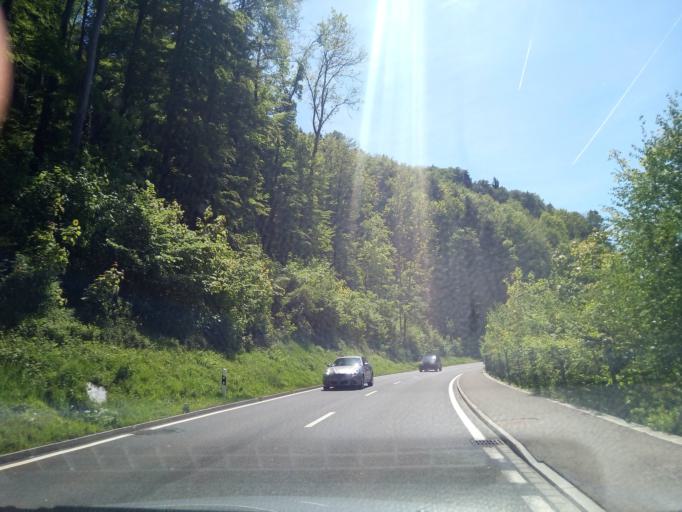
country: CH
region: Zurich
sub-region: Bezirk Horgen
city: Horgen / Allmend
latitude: 47.2186
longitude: 8.5836
